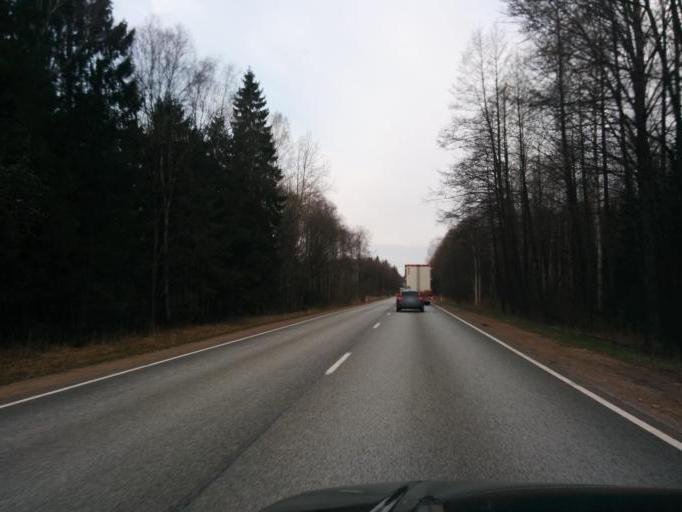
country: LV
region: Kekava
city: Balozi
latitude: 56.8197
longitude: 24.1008
